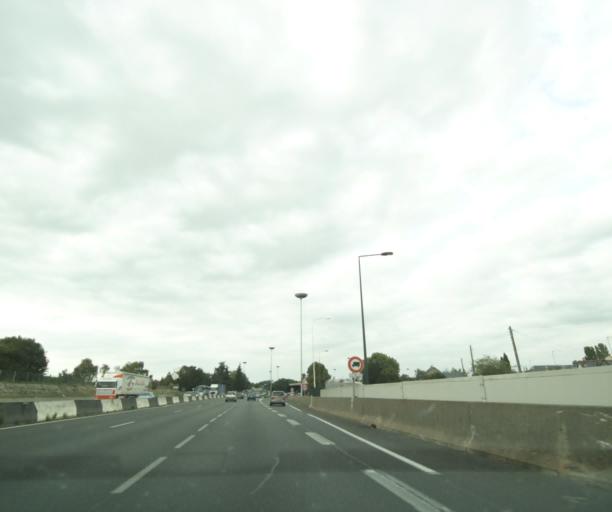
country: FR
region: Centre
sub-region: Departement d'Indre-et-Loire
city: Tours
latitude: 47.3906
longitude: 0.7068
